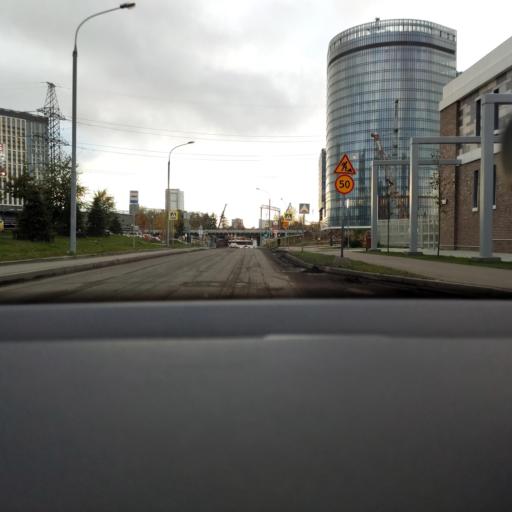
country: RU
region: Moscow
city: Sviblovo
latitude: 55.8476
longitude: 37.6347
